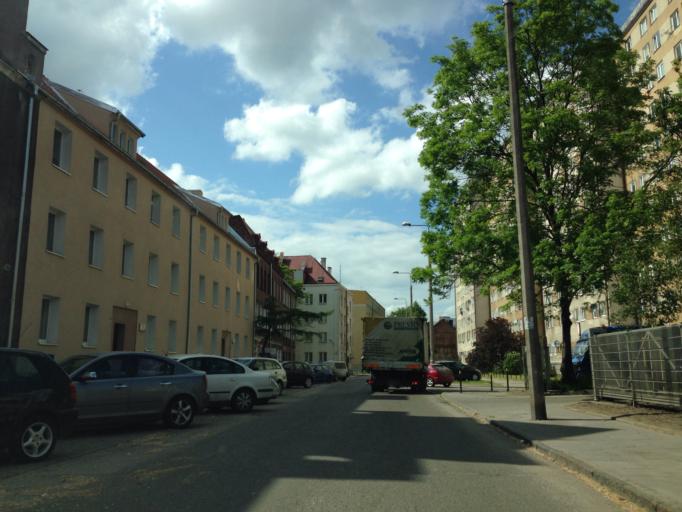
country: PL
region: Pomeranian Voivodeship
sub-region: Gdansk
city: Gdansk
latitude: 54.3778
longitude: 18.6207
